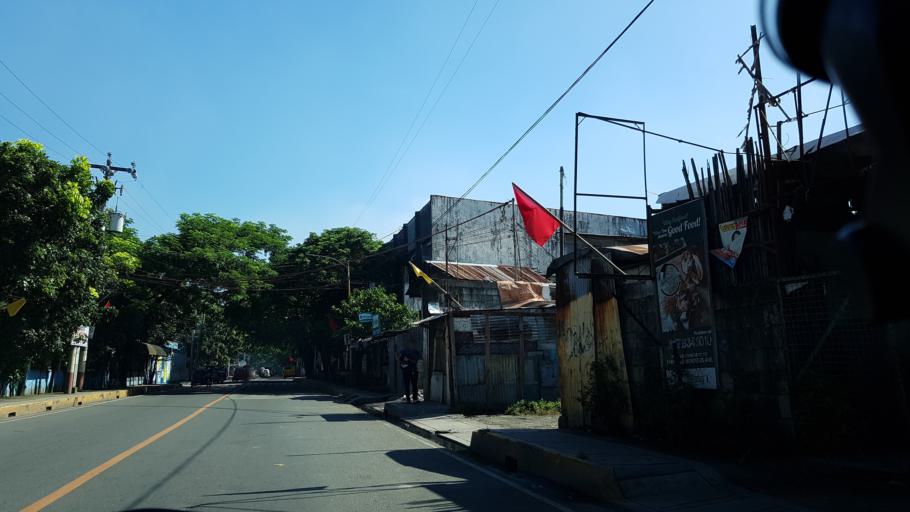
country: PH
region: Metro Manila
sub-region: Pasig
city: Pasig City
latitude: 14.5700
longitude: 121.0868
